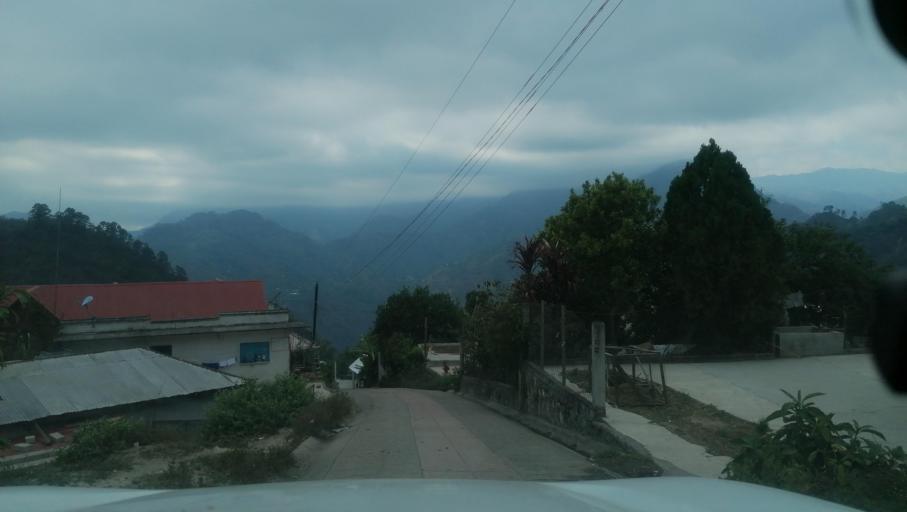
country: GT
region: San Marcos
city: Sibinal
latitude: 15.1647
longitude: -92.1559
